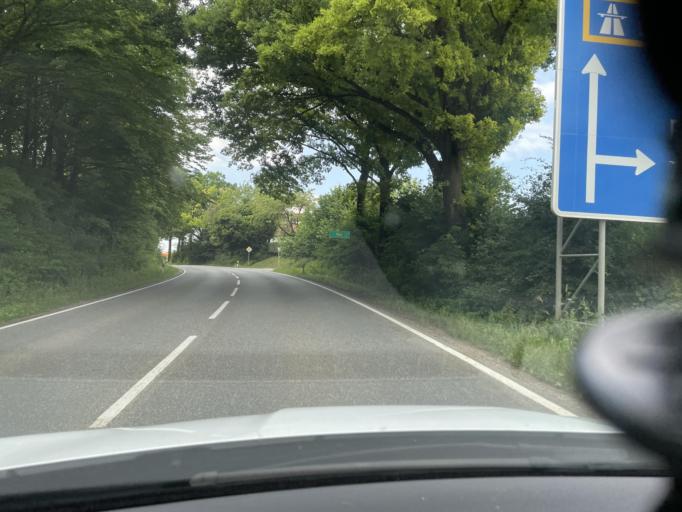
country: DE
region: Bavaria
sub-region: Upper Bavaria
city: Dorfen
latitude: 48.2563
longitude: 12.1636
